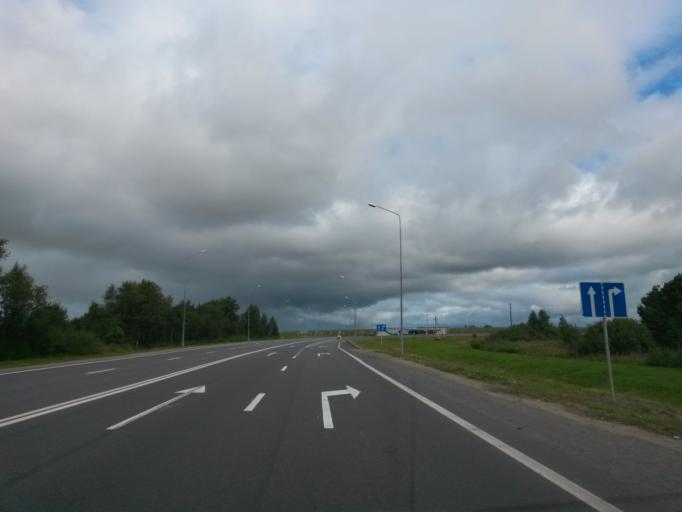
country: RU
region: Jaroslavl
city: Yaroslavl
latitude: 57.7338
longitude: 39.8970
